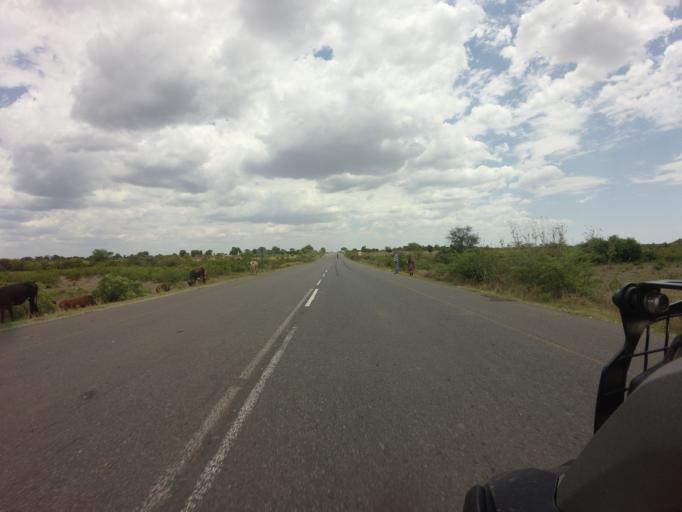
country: AO
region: Huila
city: Lubango
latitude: -15.2822
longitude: 13.8123
